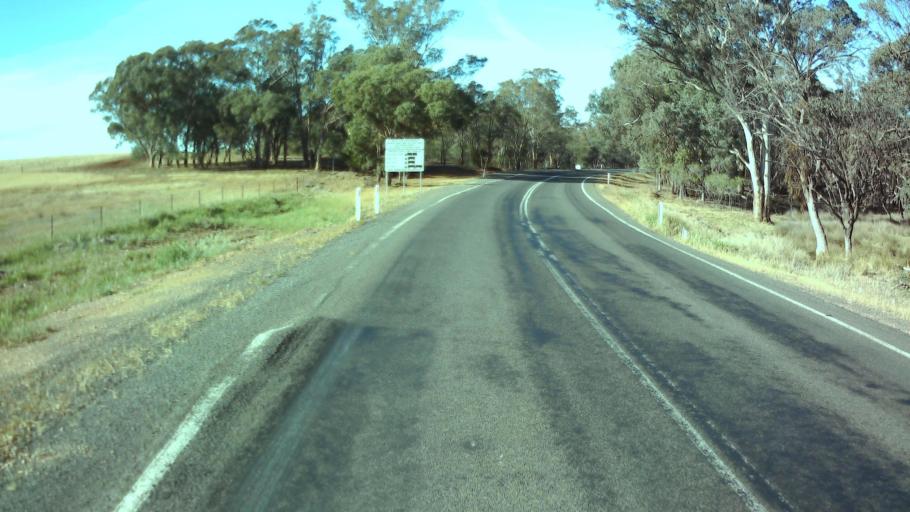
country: AU
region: New South Wales
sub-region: Weddin
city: Grenfell
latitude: -33.9990
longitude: 148.1319
